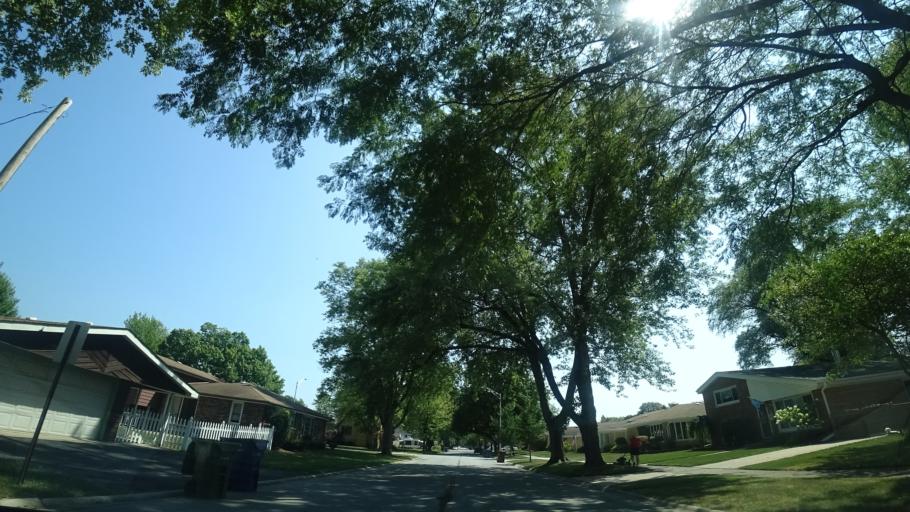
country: US
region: Illinois
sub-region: Cook County
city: Oak Lawn
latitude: 41.6996
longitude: -87.7450
